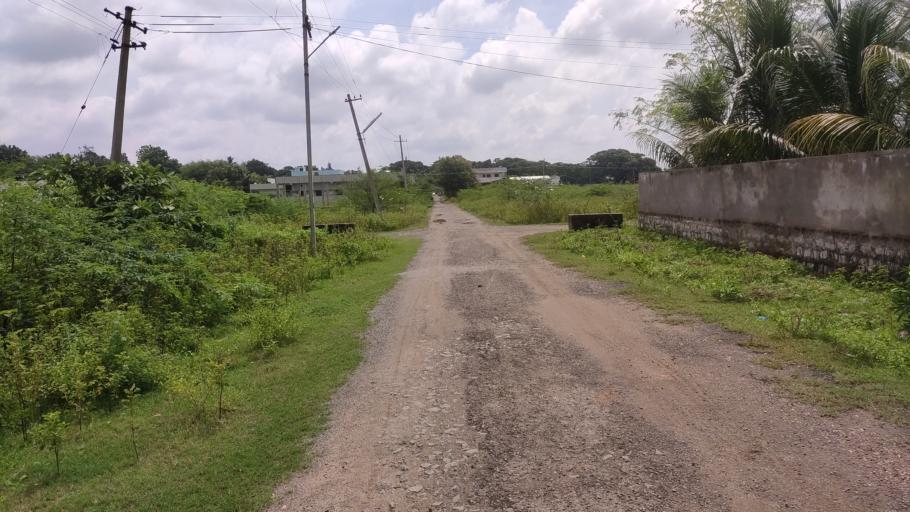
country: IN
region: Telangana
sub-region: Khammam
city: Khammam
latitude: 17.2447
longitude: 80.1935
